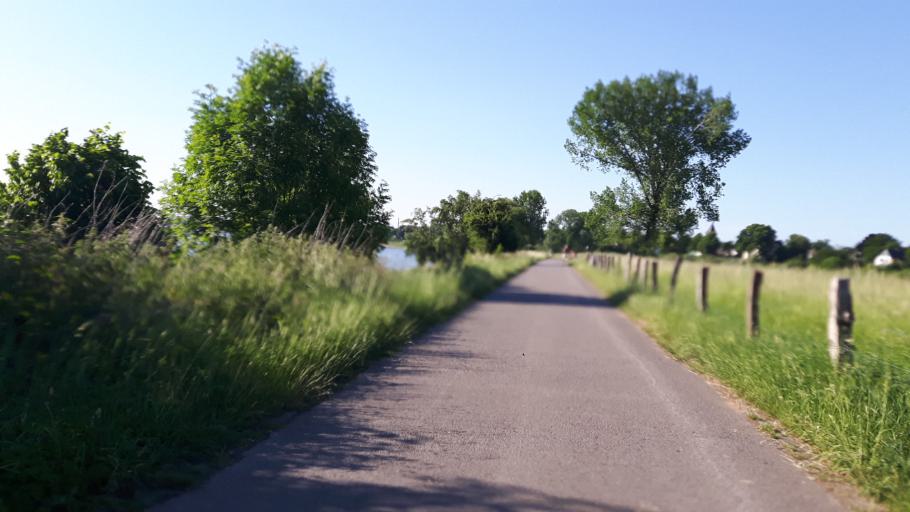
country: DE
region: North Rhine-Westphalia
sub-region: Regierungsbezirk Dusseldorf
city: Meerbusch
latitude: 51.3158
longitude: 6.7373
